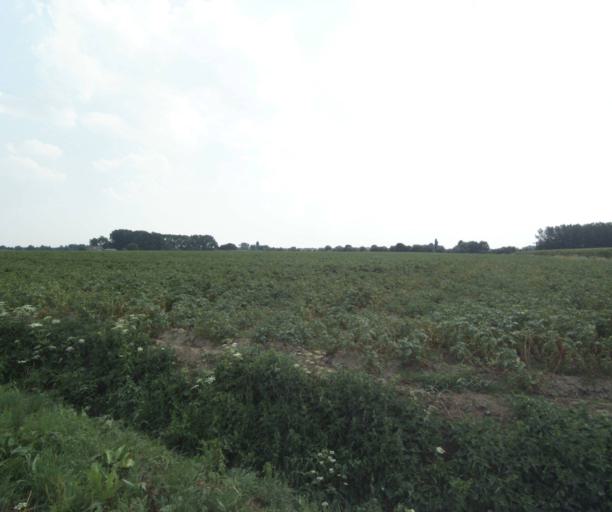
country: FR
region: Nord-Pas-de-Calais
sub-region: Departement du Nord
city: Quesnoy-sur-Deule
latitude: 50.7222
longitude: 2.9779
